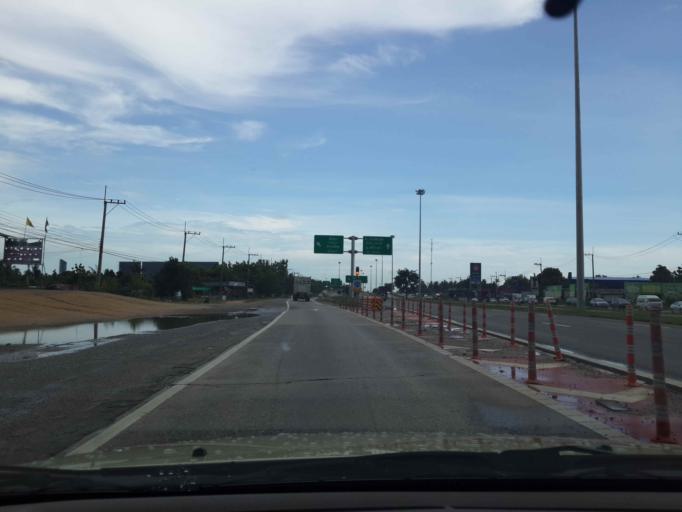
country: TH
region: Chon Buri
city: Phatthaya
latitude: 12.9581
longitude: 100.9848
